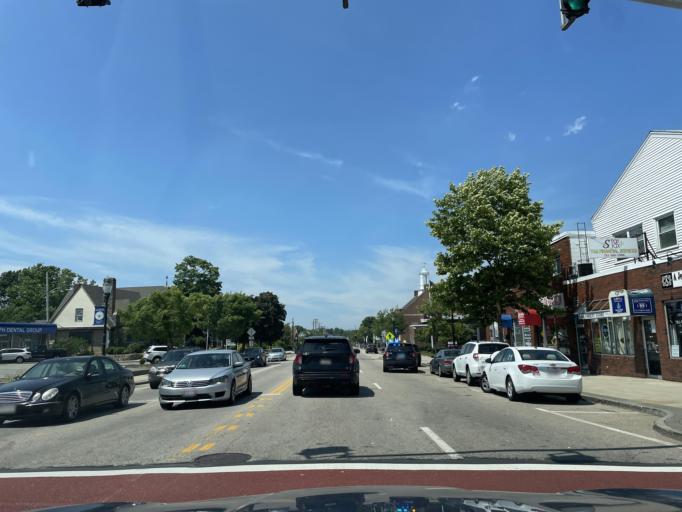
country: US
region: Massachusetts
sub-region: Norfolk County
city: Randolph
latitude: 42.1641
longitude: -71.0424
